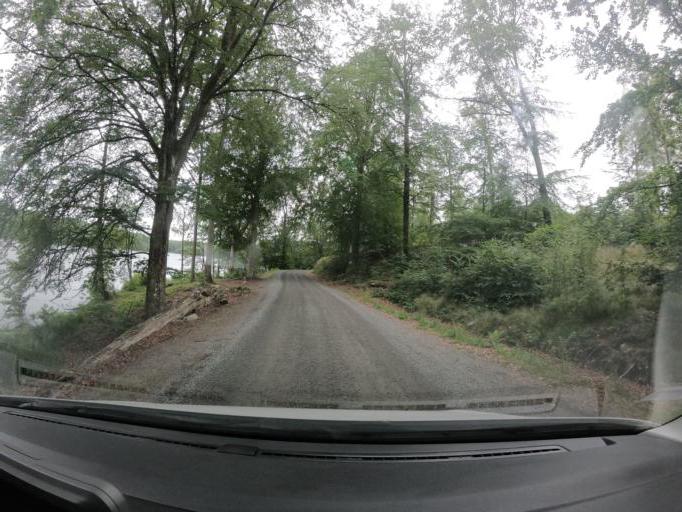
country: SE
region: Skane
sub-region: Hoors Kommun
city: Hoeoer
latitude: 55.9885
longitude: 13.4887
